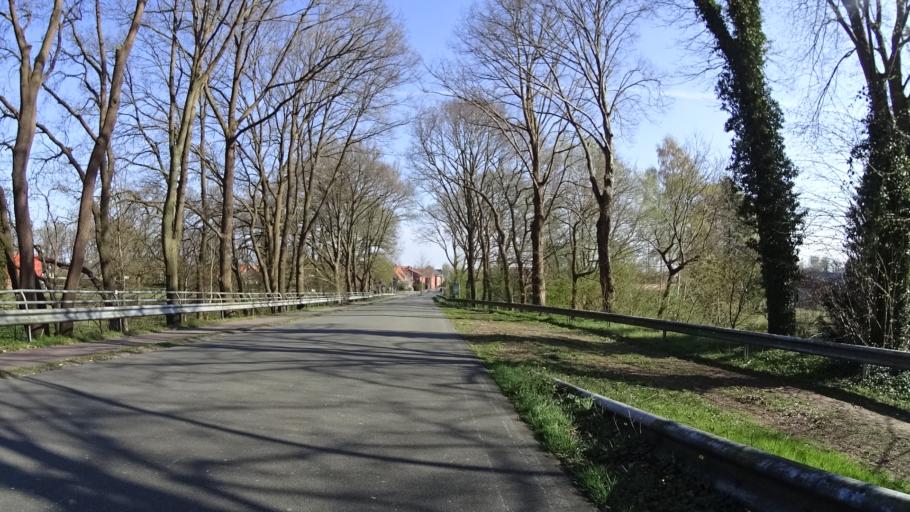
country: DE
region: Lower Saxony
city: Dorpen
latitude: 52.9688
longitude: 7.3180
